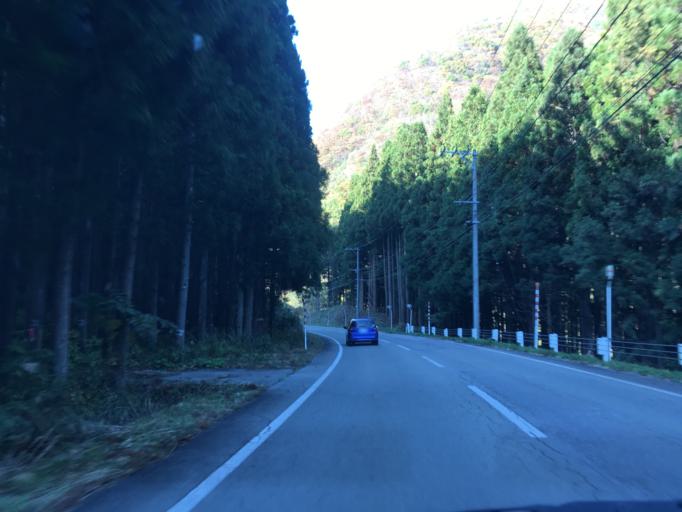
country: JP
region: Fukushima
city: Inawashiro
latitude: 37.2925
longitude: 139.9612
